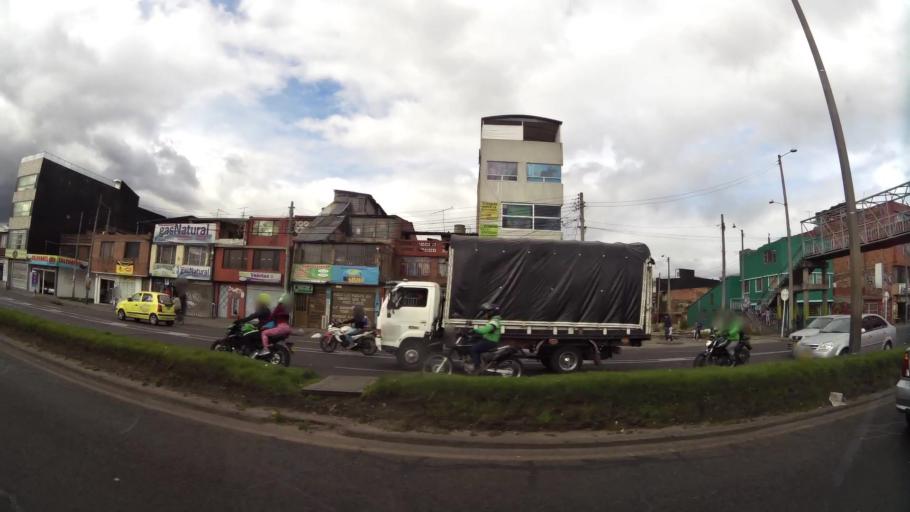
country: CO
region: Bogota D.C.
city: Bogota
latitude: 4.6075
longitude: -74.1274
